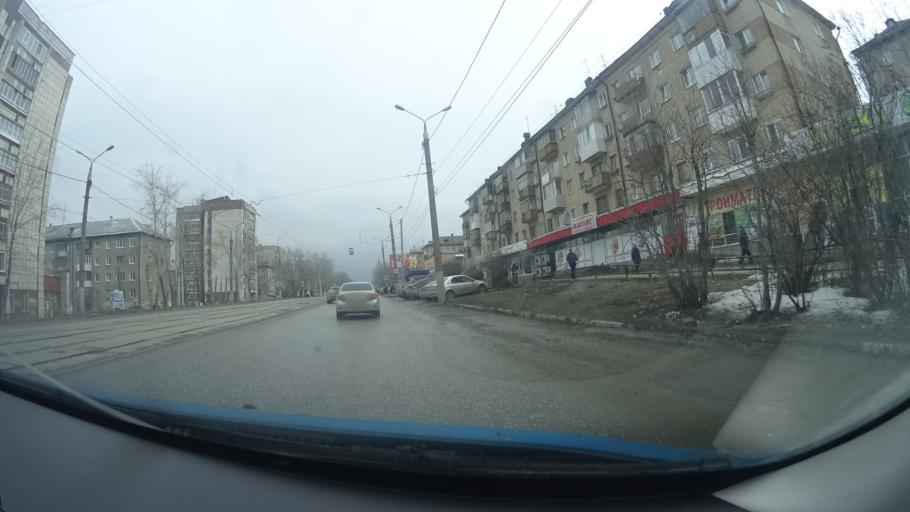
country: RU
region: Perm
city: Kondratovo
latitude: 57.9705
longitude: 56.1600
